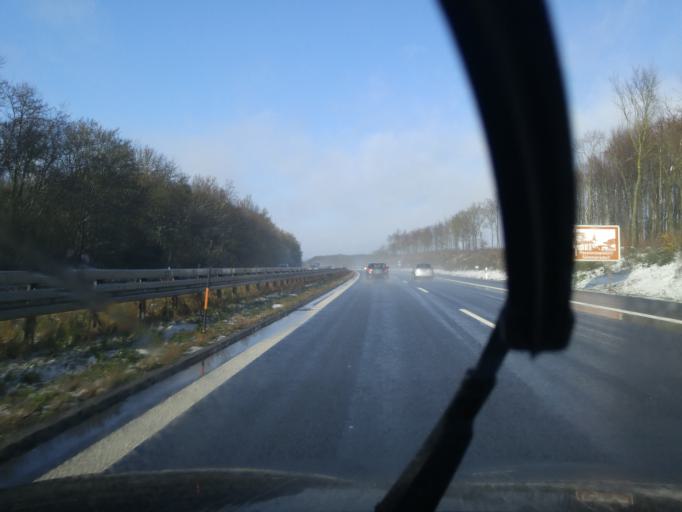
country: DE
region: Bavaria
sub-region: Regierungsbezirk Unterfranken
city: Wasserlosen
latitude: 50.0411
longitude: 10.0664
